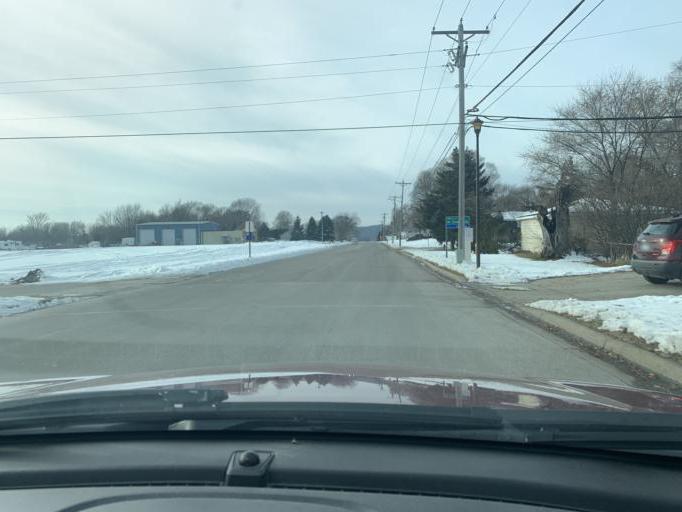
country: US
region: Minnesota
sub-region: Washington County
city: Saint Paul Park
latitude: 44.8262
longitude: -92.9796
